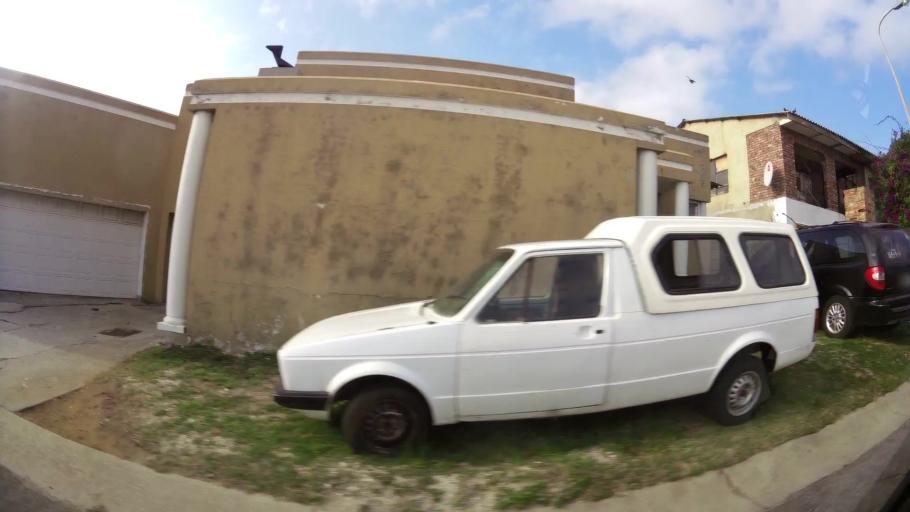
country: ZA
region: Eastern Cape
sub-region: Nelson Mandela Bay Metropolitan Municipality
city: Port Elizabeth
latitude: -33.9230
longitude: 25.5535
